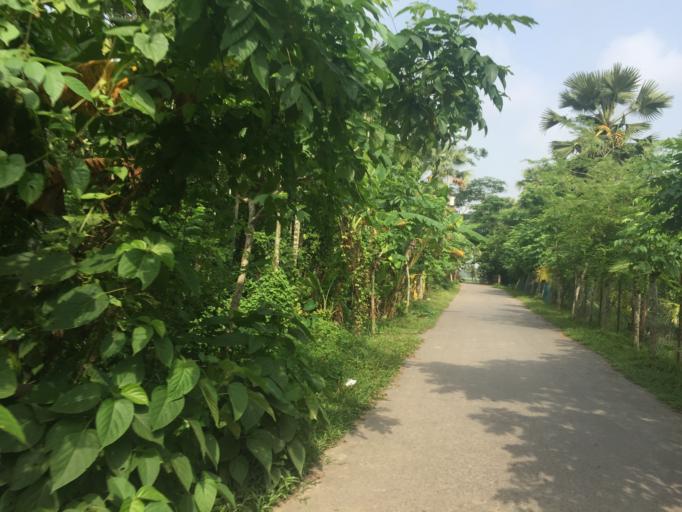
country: BD
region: Barisal
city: Mathba
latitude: 22.2094
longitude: 89.9325
